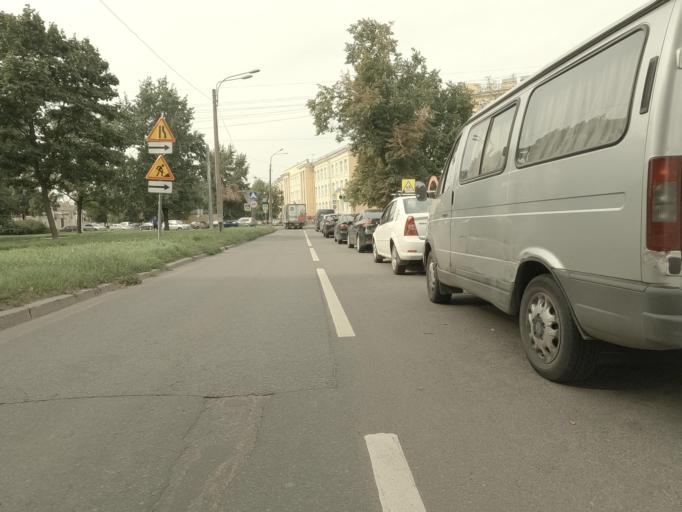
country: RU
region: St.-Petersburg
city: Admiralteisky
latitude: 59.9114
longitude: 30.2875
